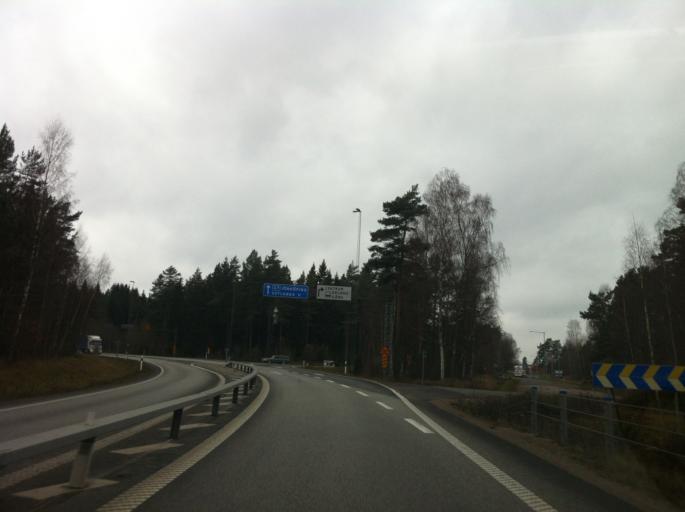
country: SE
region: Joenkoeping
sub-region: Vetlanda Kommun
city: Vetlanda
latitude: 57.4239
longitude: 15.1203
